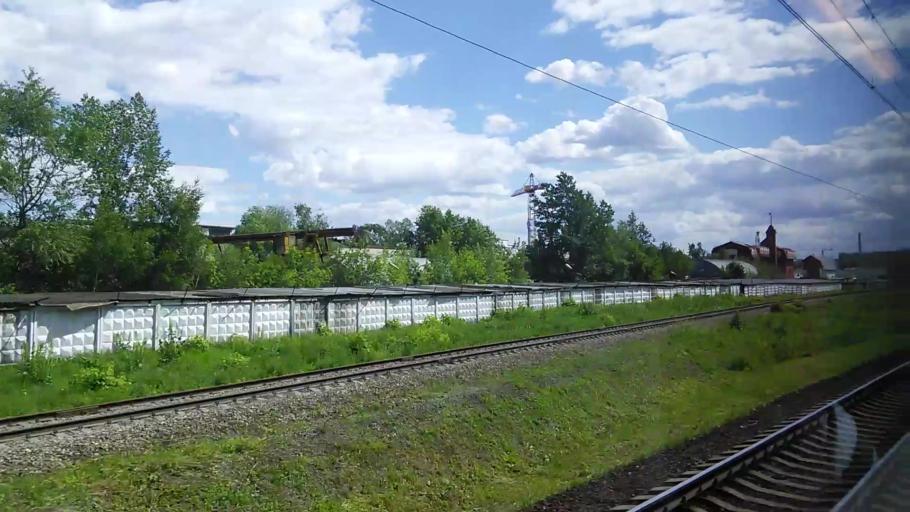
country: RU
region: Moscow
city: Slobodka
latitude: 55.8603
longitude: 37.5747
